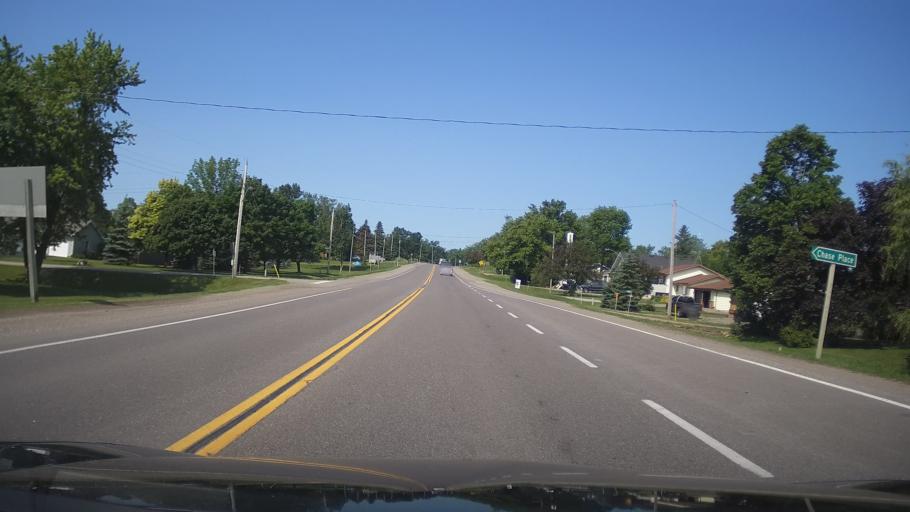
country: CA
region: Ontario
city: Omemee
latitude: 44.3477
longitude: -78.8076
